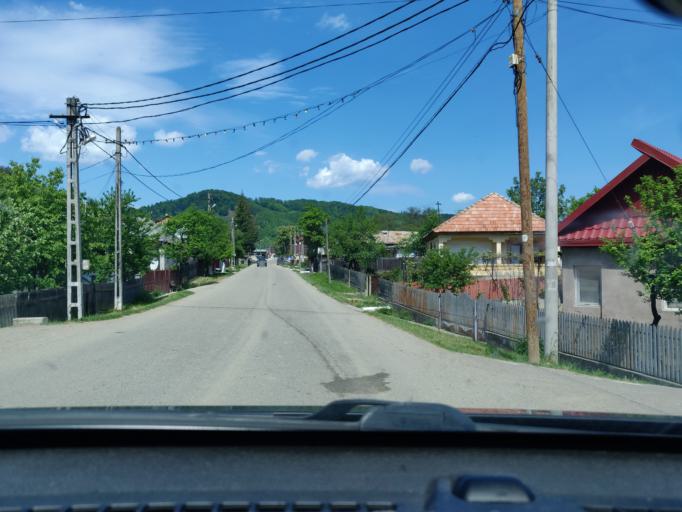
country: RO
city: Vizantea-Manastireasca
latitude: 45.9851
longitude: 26.7785
